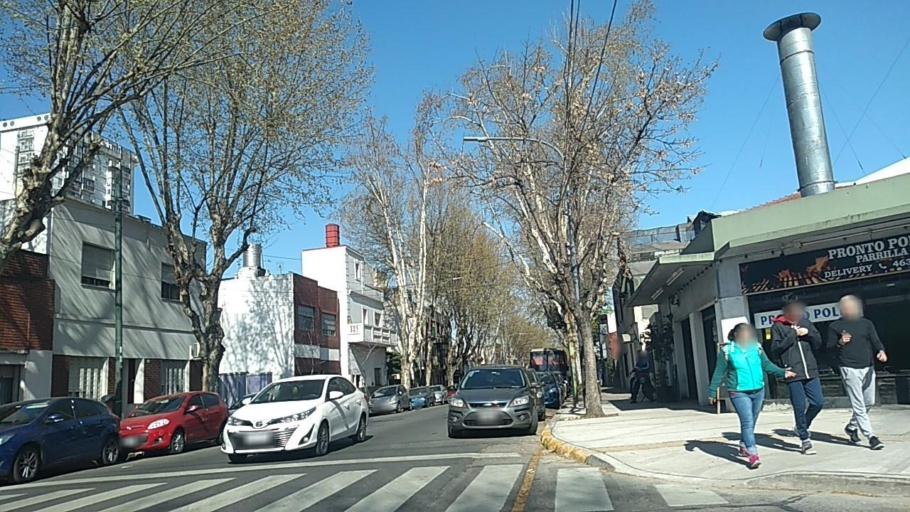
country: AR
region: Buenos Aires F.D.
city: Villa Santa Rita
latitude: -34.6106
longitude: -58.4892
